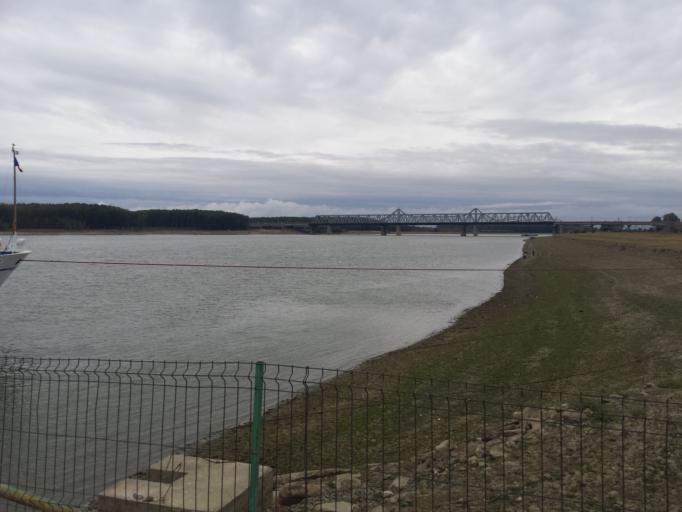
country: RO
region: Ialomita
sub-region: Municipiul Fetesti
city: Vlasca
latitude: 44.3902
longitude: 27.8565
